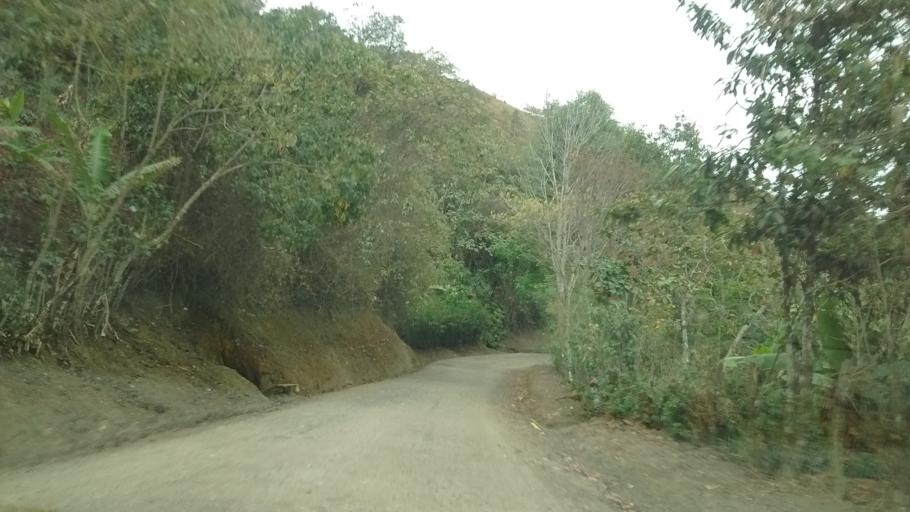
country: CO
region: Cauca
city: Almaguer
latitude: 1.8509
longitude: -76.9235
